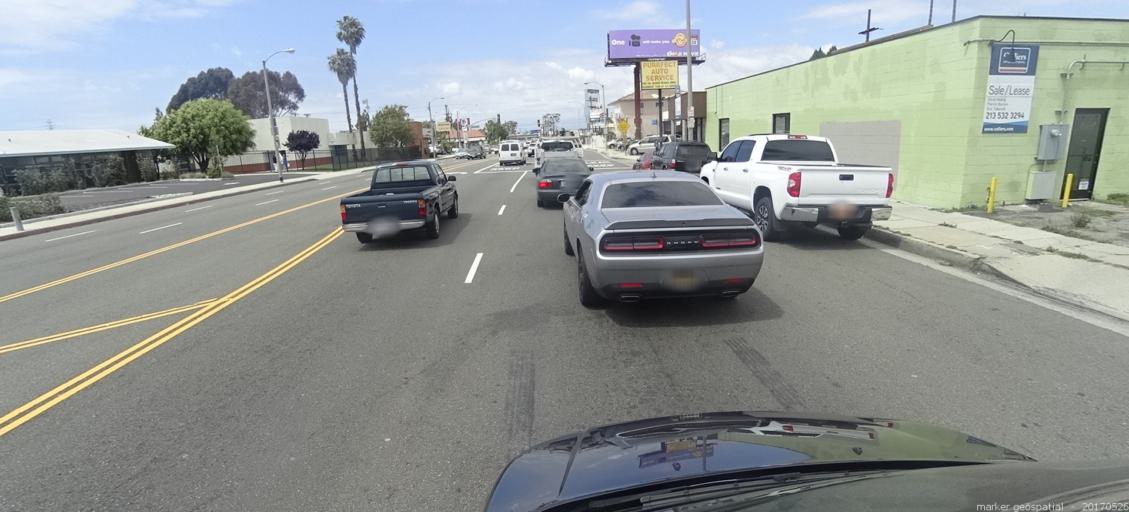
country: US
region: California
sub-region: Los Angeles County
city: Lawndale
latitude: 33.8860
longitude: -118.3613
